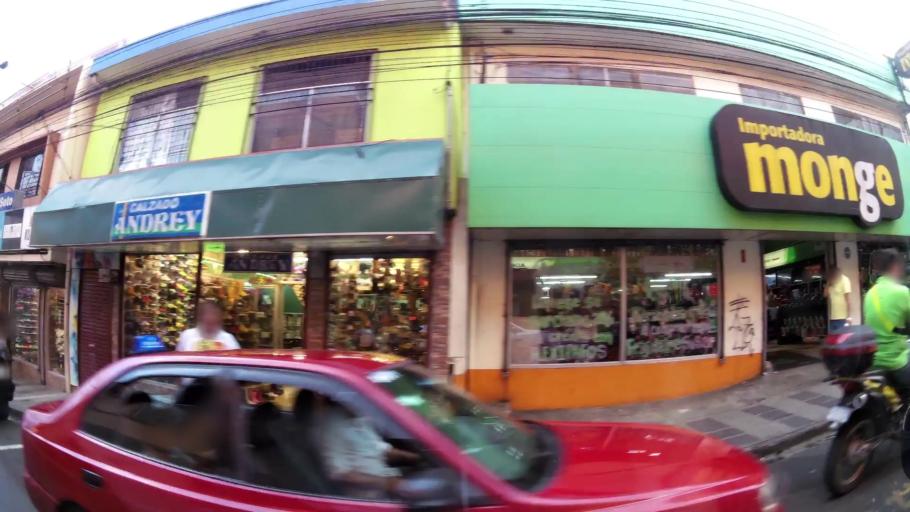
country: CR
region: Heredia
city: Heredia
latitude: 9.9952
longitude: -84.1176
